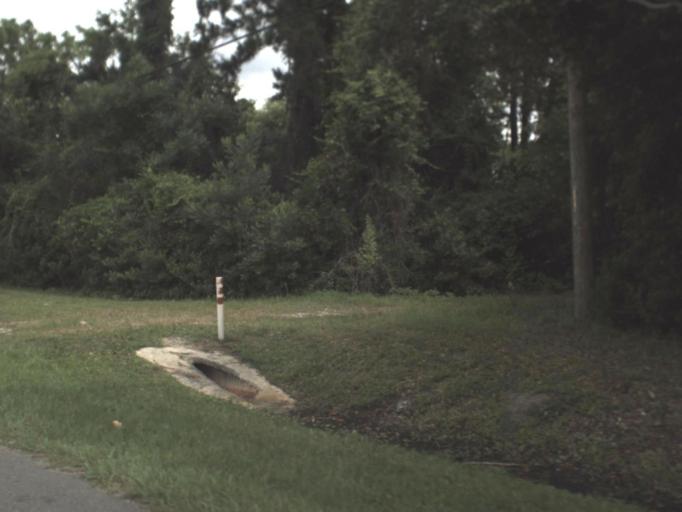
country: US
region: Florida
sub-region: Duval County
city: Atlantic Beach
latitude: 30.4157
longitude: -81.5268
